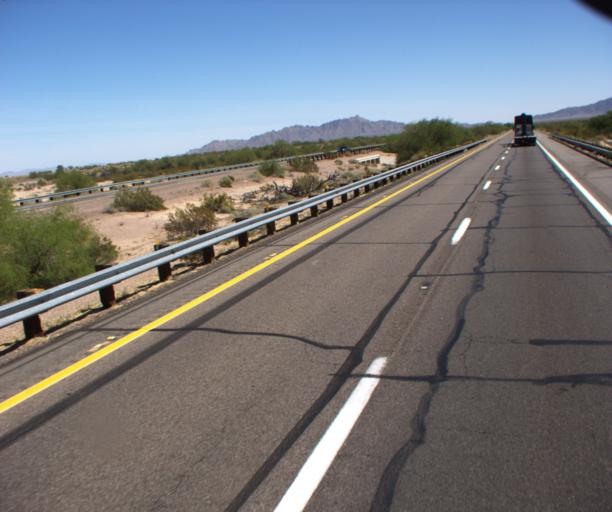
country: US
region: Arizona
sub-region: Yuma County
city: Wellton
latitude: 32.7041
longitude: -113.8828
